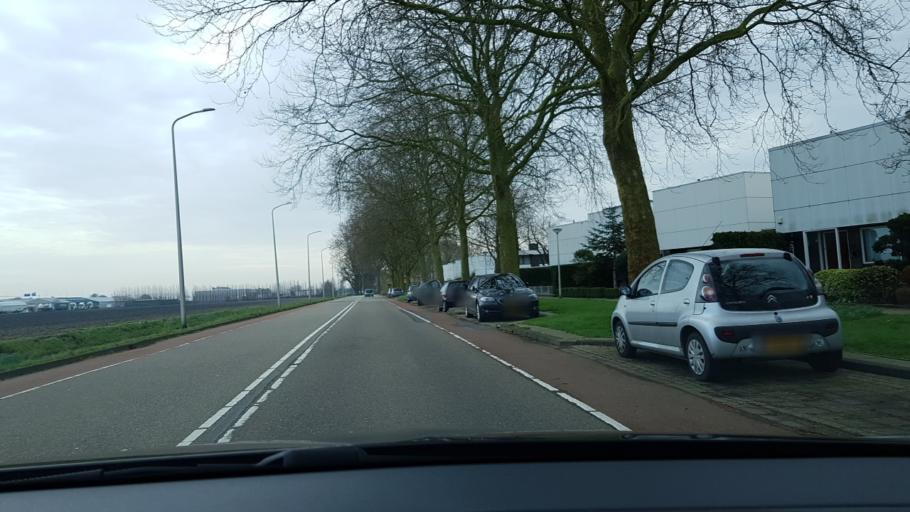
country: NL
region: North Holland
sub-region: Gemeente Uithoorn
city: Uithoorn
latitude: 52.2549
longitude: 4.8169
